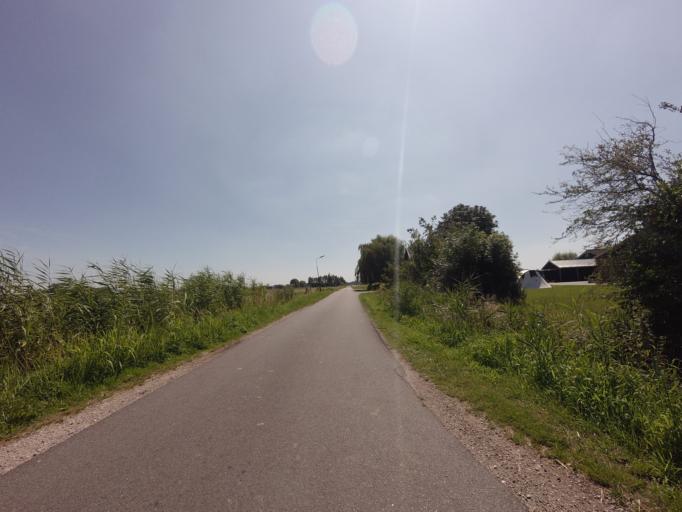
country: NL
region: Utrecht
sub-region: Stichtse Vecht
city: Maarssen
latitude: 52.1641
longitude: 5.0643
